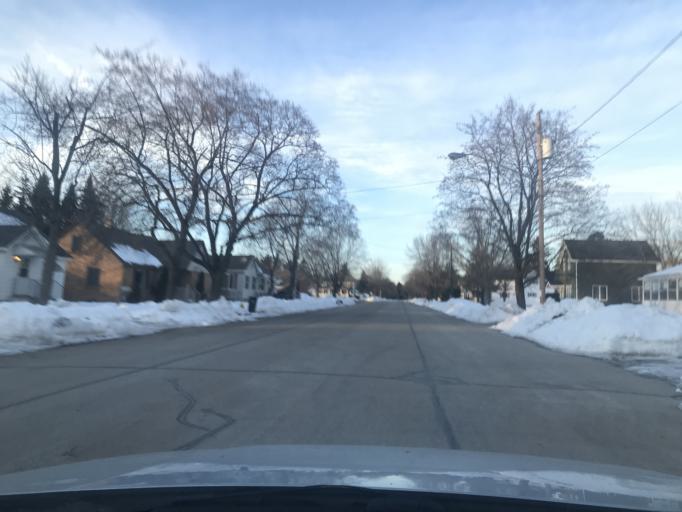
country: US
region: Wisconsin
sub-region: Marinette County
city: Peshtigo
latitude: 45.0535
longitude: -87.7402
